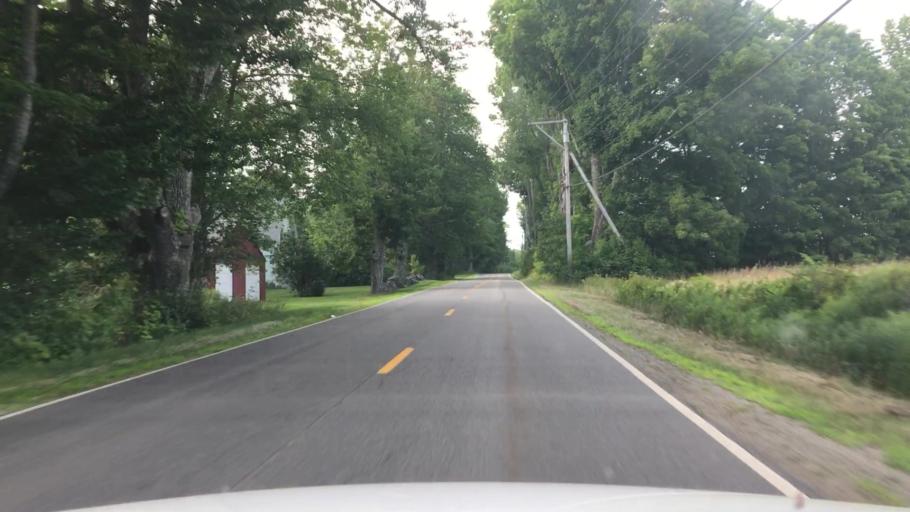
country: US
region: Maine
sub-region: Lincoln County
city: Waldoboro
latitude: 44.1346
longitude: -69.3704
